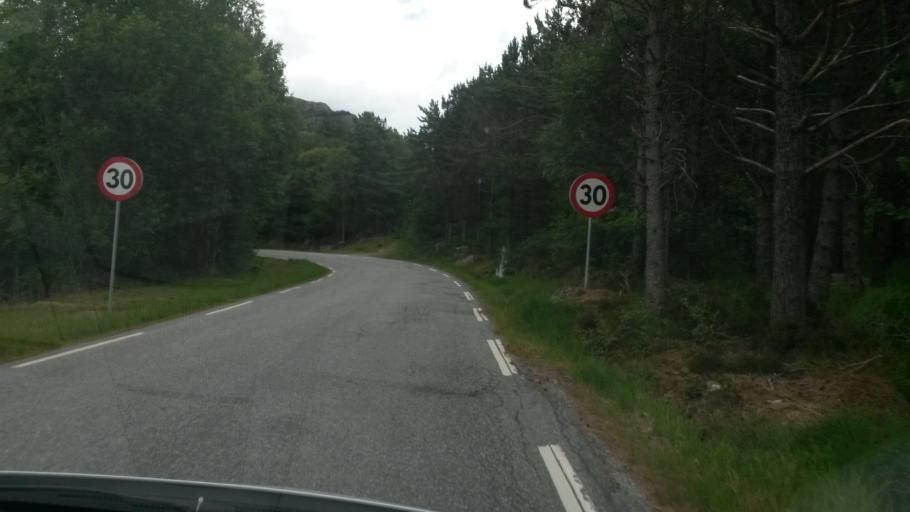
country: NO
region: Rogaland
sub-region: Sandnes
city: Sandnes
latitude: 58.8956
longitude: 5.7753
